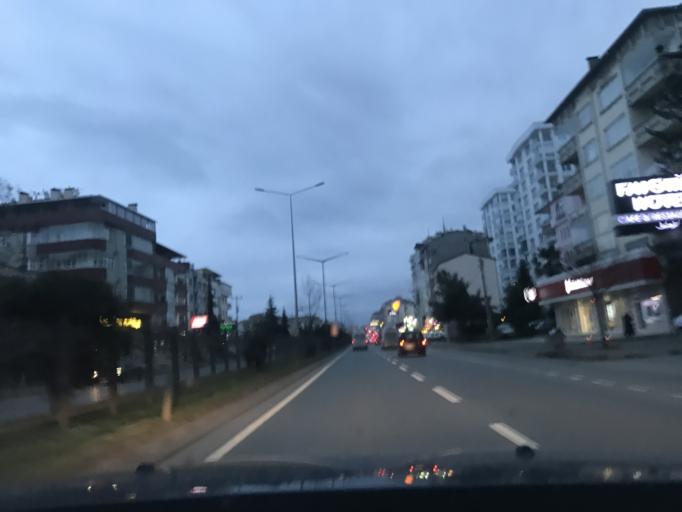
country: TR
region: Trabzon
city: Akcaabat
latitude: 41.0141
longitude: 39.6023
